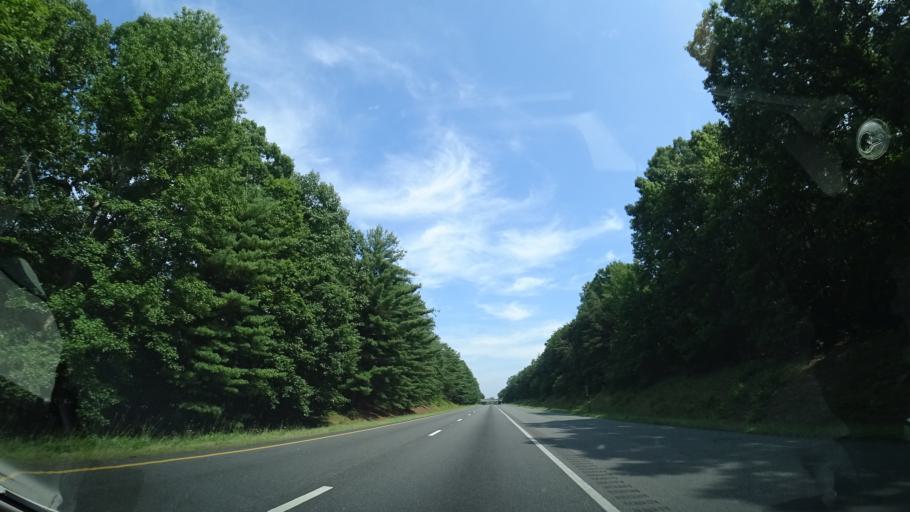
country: US
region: Virginia
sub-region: Louisa County
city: Louisa
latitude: 37.9076
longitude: -78.0598
